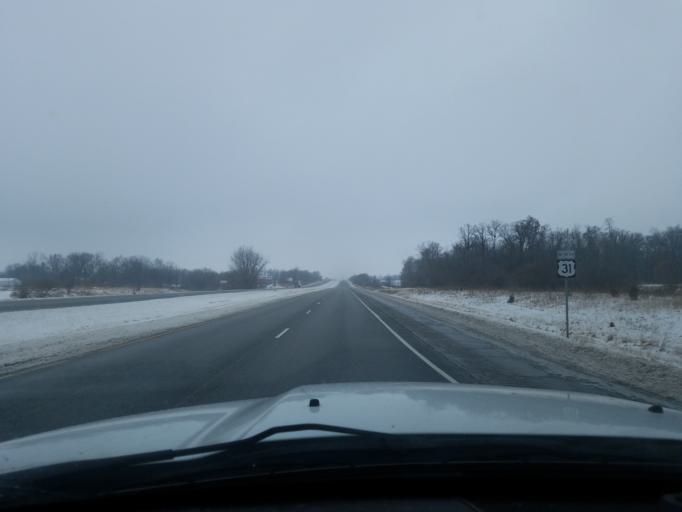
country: US
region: Indiana
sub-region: Fulton County
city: Rochester
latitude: 40.9609
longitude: -86.1682
